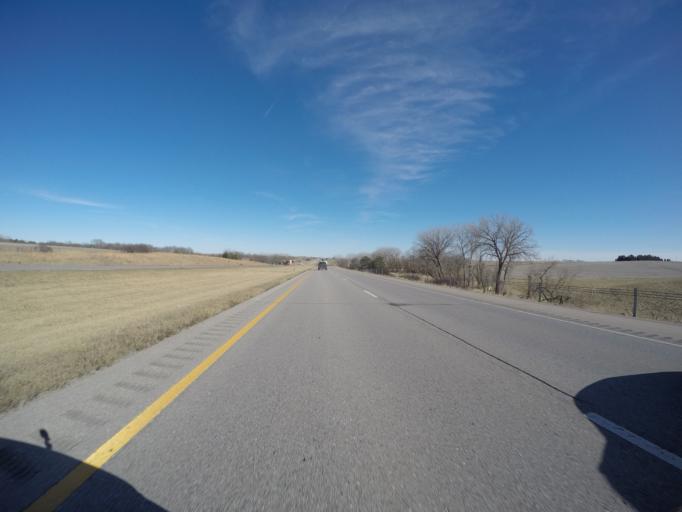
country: US
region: Nebraska
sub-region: Seward County
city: Milford
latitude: 40.8212
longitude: -96.9718
